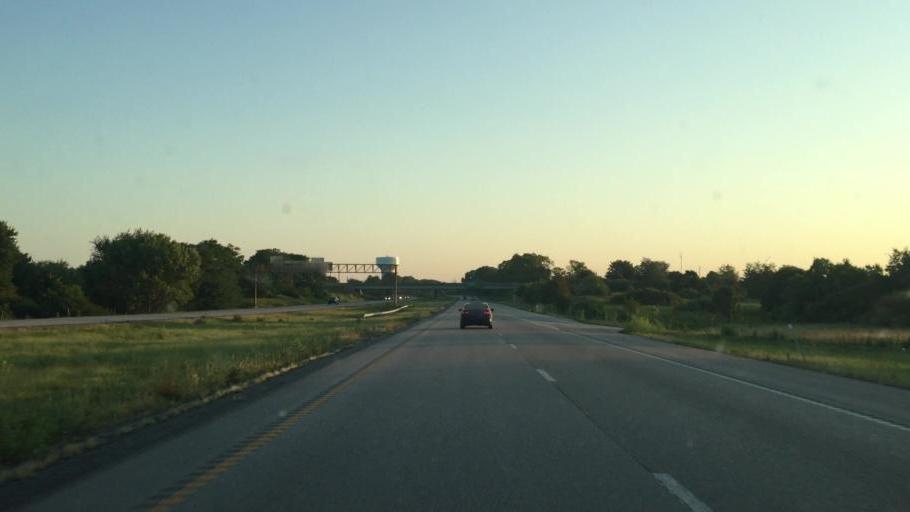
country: US
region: Missouri
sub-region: Clay County
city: Pleasant Valley
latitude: 39.2994
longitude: -94.5100
